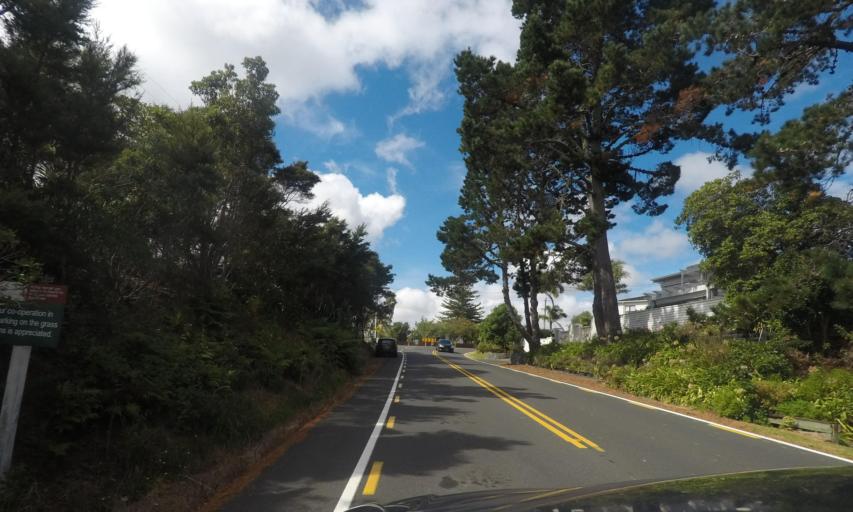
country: NZ
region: Auckland
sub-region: Auckland
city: Rosebank
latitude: -36.7815
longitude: 174.6504
